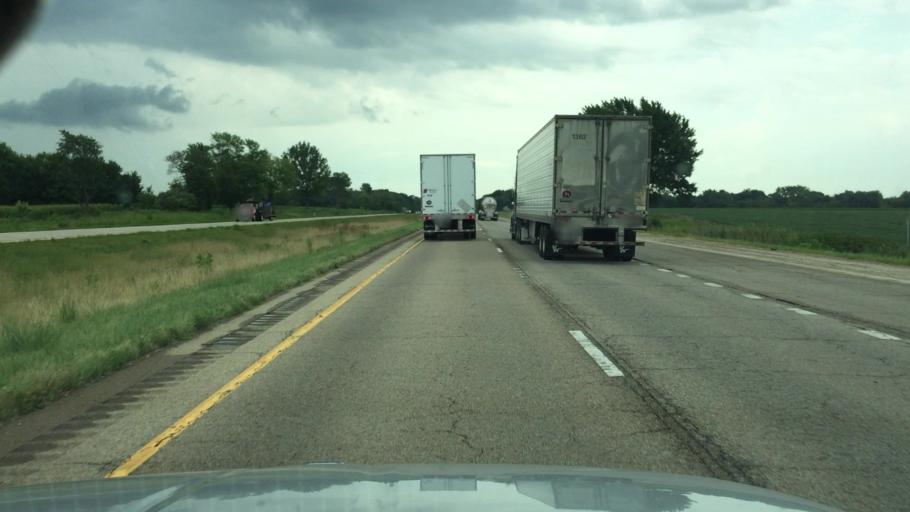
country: US
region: Illinois
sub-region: Peoria County
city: Hanna City
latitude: 40.7725
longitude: -89.7491
